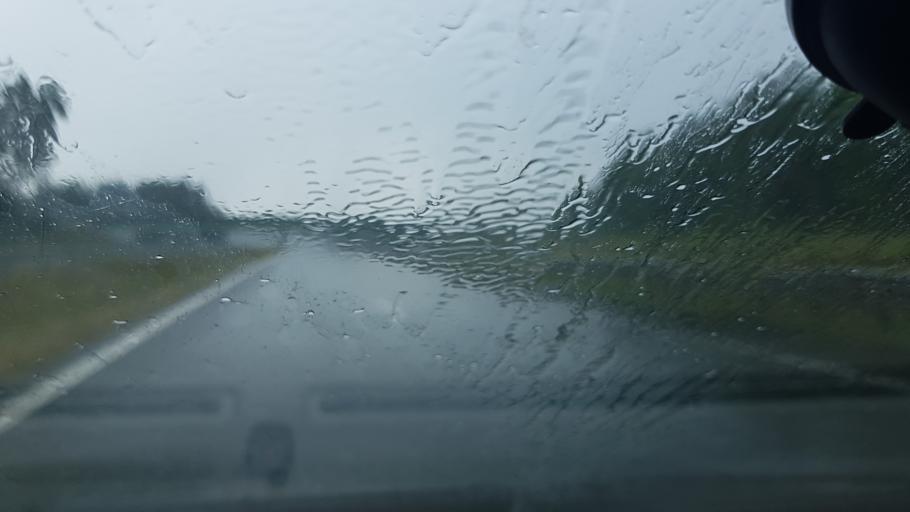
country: PL
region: Warmian-Masurian Voivodeship
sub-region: Powiat olsztynski
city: Olsztynek
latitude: 53.4582
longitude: 20.3216
